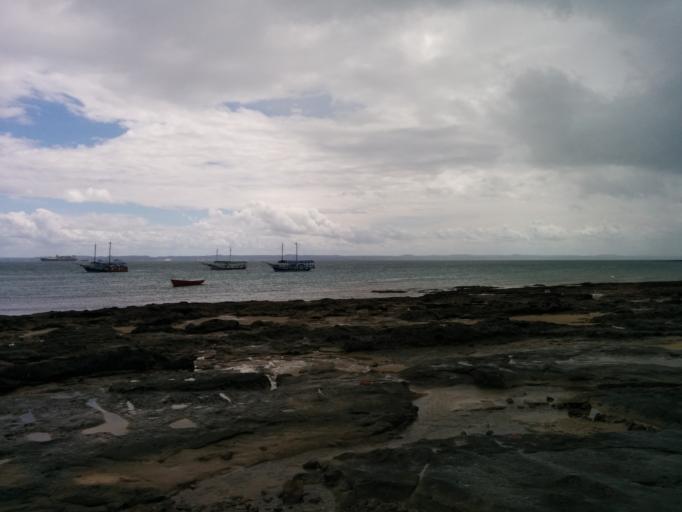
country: BR
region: Bahia
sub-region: Madre De Deus
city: Madre de Deus
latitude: -12.8148
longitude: -38.6416
